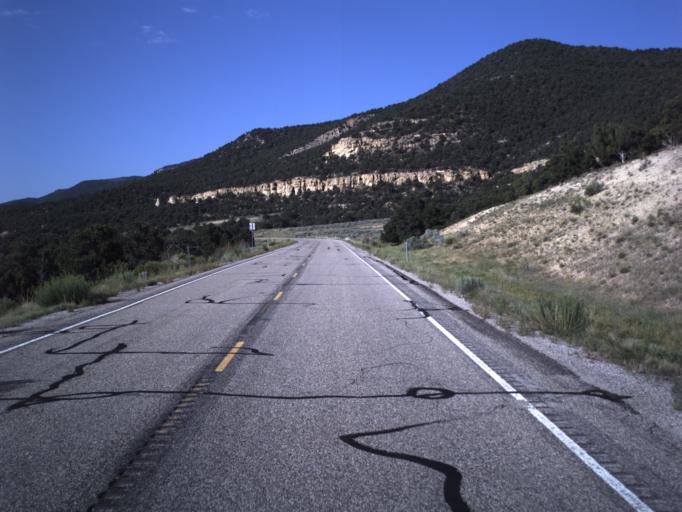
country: US
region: Utah
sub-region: Wayne County
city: Loa
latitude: 38.7473
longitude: -111.3922
